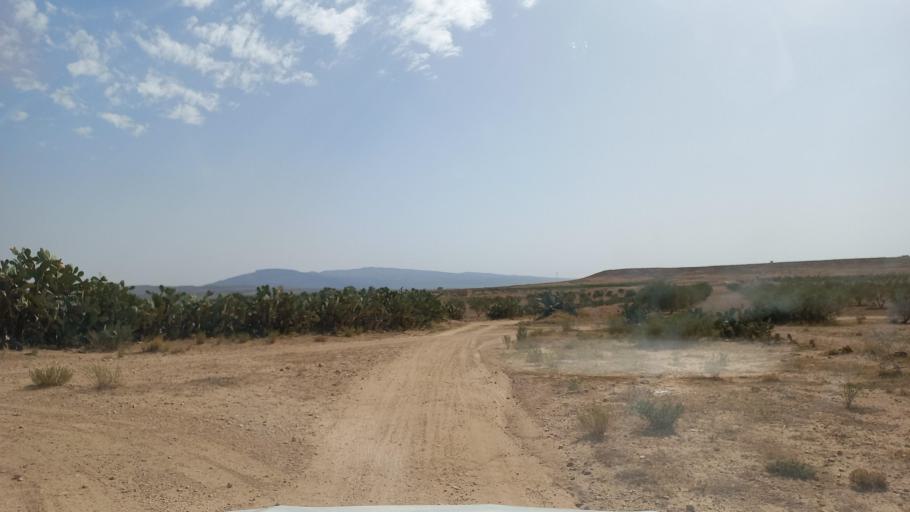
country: TN
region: Al Qasrayn
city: Kasserine
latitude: 35.2762
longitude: 8.9694
